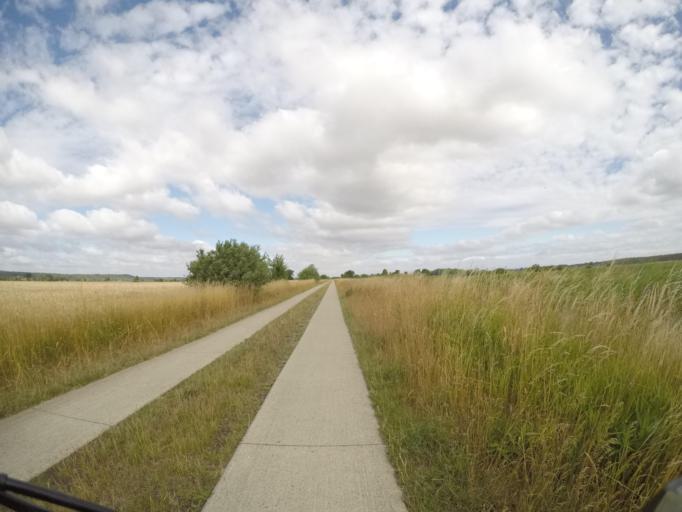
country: DE
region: Lower Saxony
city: Hitzacker
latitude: 53.1746
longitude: 11.0482
